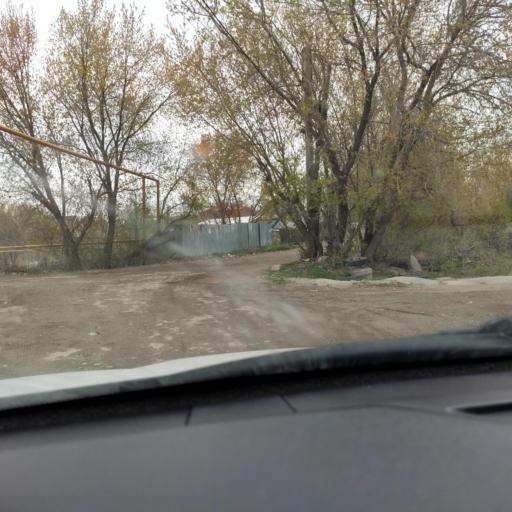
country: RU
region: Samara
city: Petra-Dubrava
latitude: 53.2563
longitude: 50.3439
